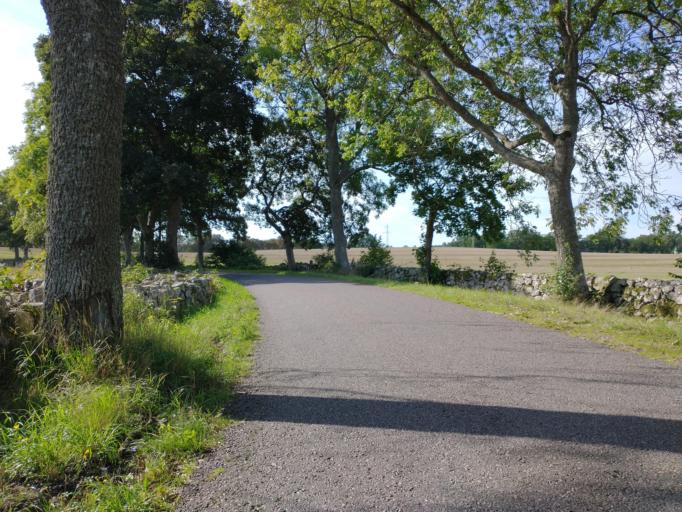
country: SE
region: Kalmar
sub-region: Kalmar Kommun
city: Lindsdal
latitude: 56.7799
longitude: 16.3207
